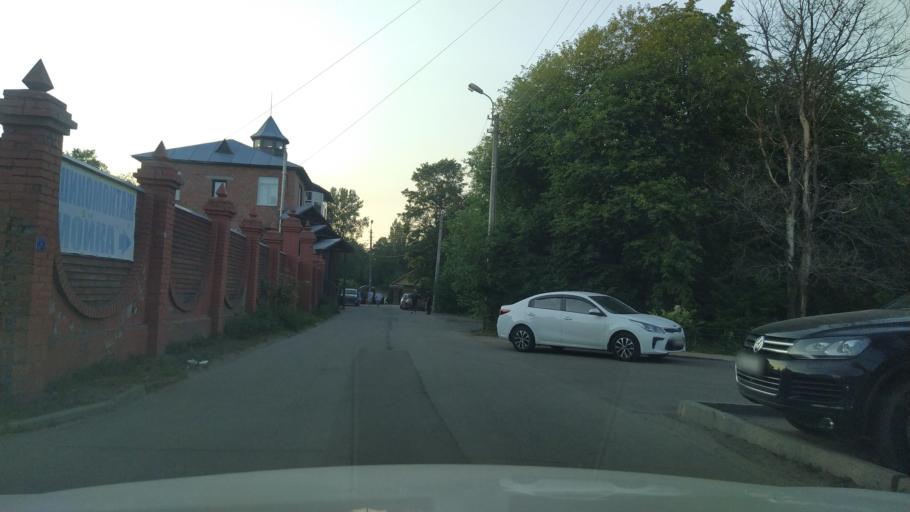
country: RU
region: St.-Petersburg
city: Sestroretsk
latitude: 60.0921
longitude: 29.9481
